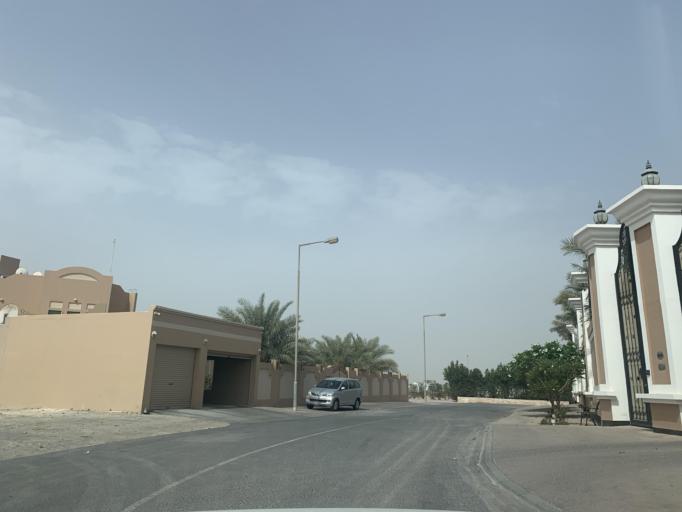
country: BH
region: Central Governorate
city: Madinat Hamad
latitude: 26.1441
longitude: 50.5123
